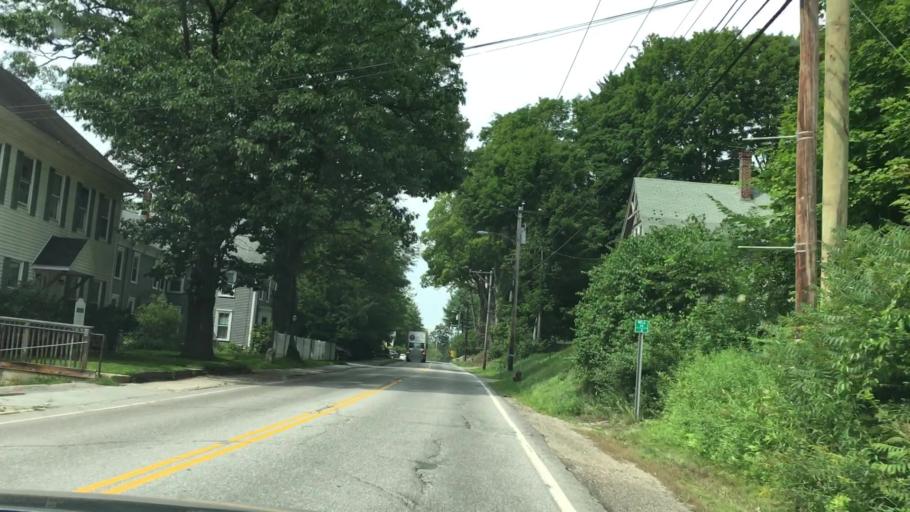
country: US
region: New Hampshire
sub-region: Hillsborough County
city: Peterborough
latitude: 42.8724
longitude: -71.9485
